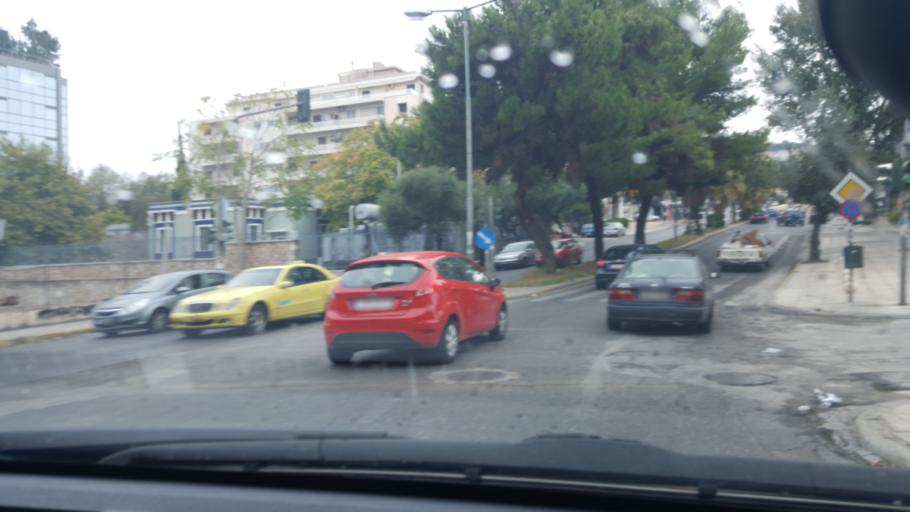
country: GR
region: Attica
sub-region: Nomarchia Athinas
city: Neo Psychiko
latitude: 37.9970
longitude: 23.7703
